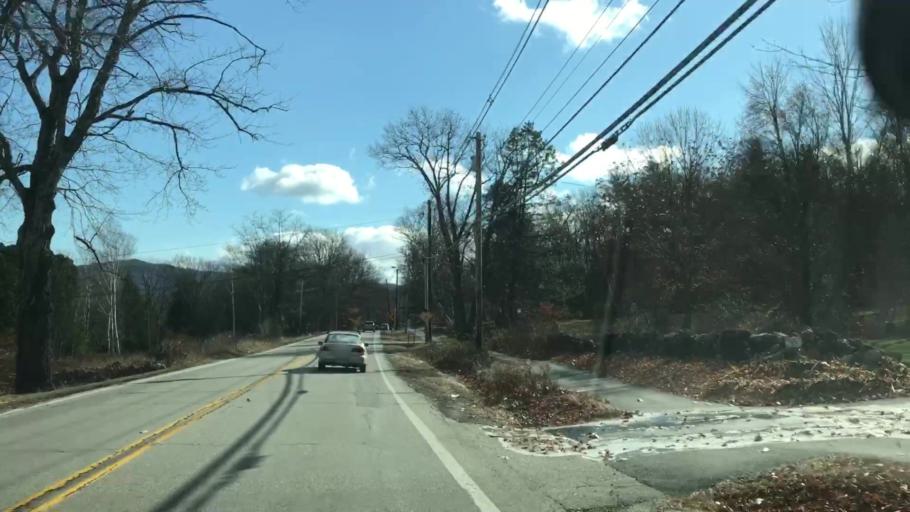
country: US
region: New Hampshire
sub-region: Carroll County
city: Wolfeboro
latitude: 43.5689
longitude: -71.1807
